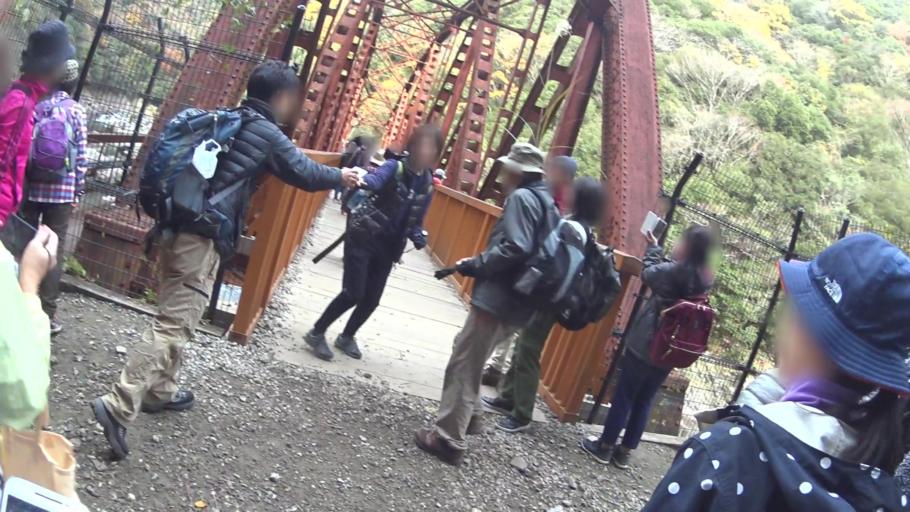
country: JP
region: Hyogo
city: Takarazuka
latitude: 34.8469
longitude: 135.3153
